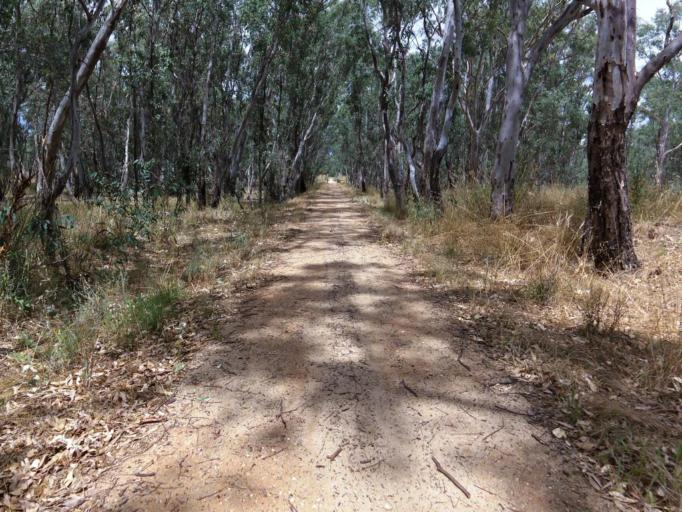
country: AU
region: Victoria
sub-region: Greater Bendigo
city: Kennington
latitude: -36.8729
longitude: 144.6314
